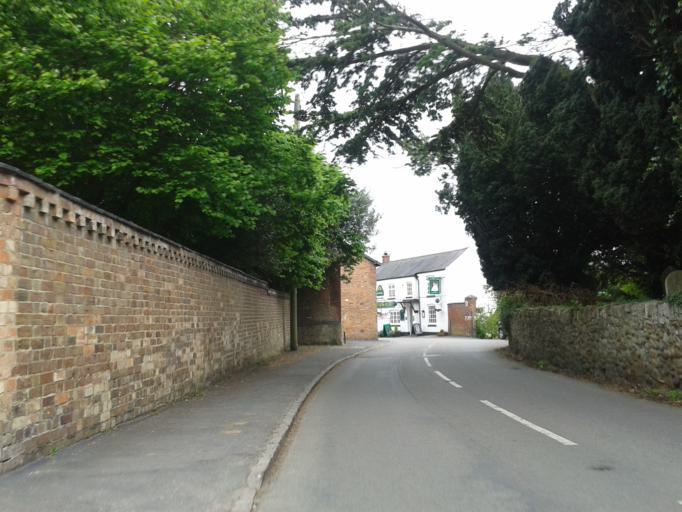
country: GB
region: England
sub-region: Leicestershire
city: Kibworth Harcourt
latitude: 52.5202
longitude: -1.0317
